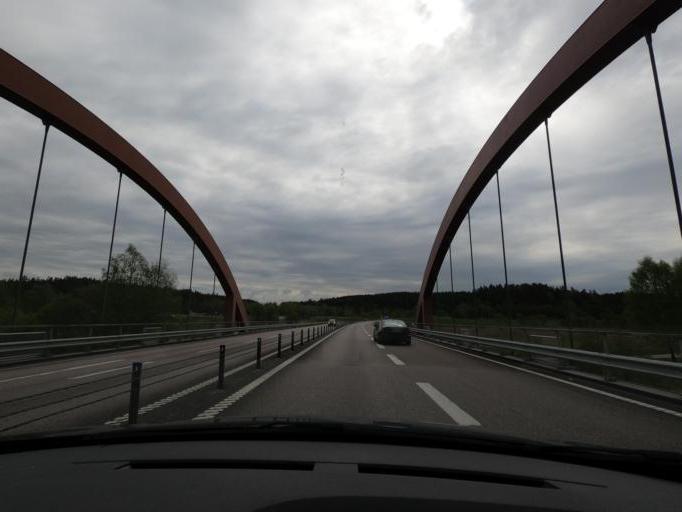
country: SE
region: Vaestra Goetaland
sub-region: Boras Kommun
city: Boras
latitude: 57.6971
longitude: 12.9121
